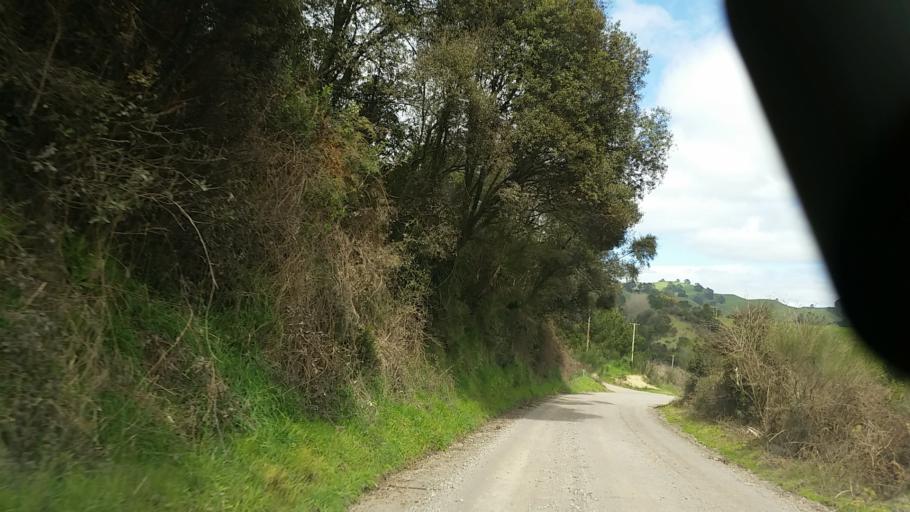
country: NZ
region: Bay of Plenty
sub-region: Rotorua District
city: Rotorua
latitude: -38.3752
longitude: 176.2051
